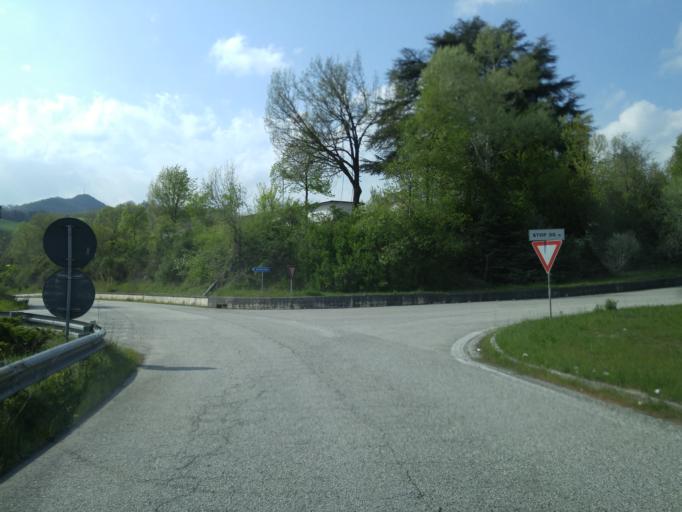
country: IT
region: The Marches
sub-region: Provincia di Pesaro e Urbino
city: Acqualagna
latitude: 43.6390
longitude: 12.6944
